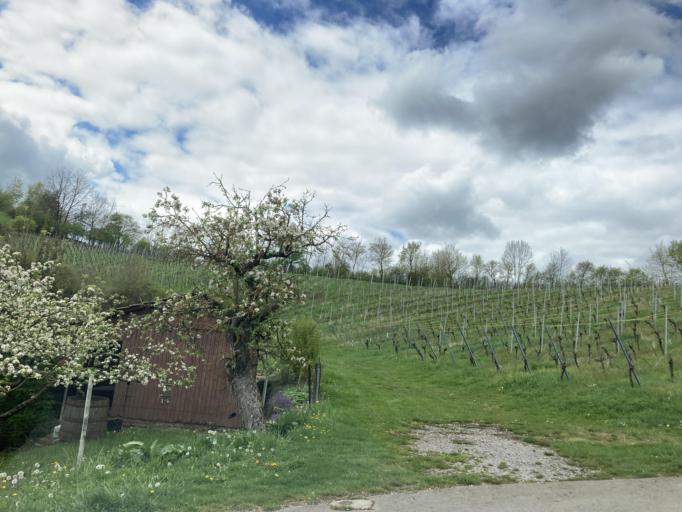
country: DE
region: Baden-Wuerttemberg
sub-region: Tuebingen Region
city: Rottenburg
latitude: 48.5076
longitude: 8.9858
